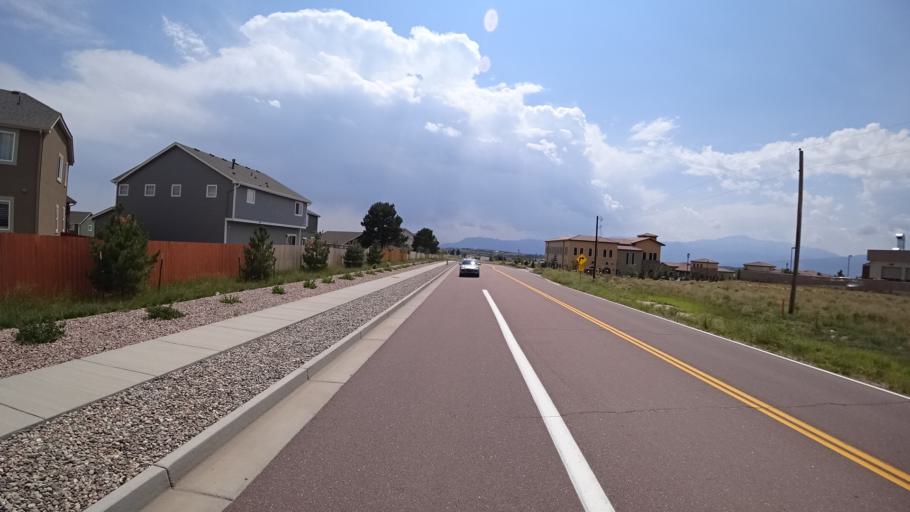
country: US
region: Colorado
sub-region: El Paso County
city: Cimarron Hills
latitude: 38.9333
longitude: -104.7112
